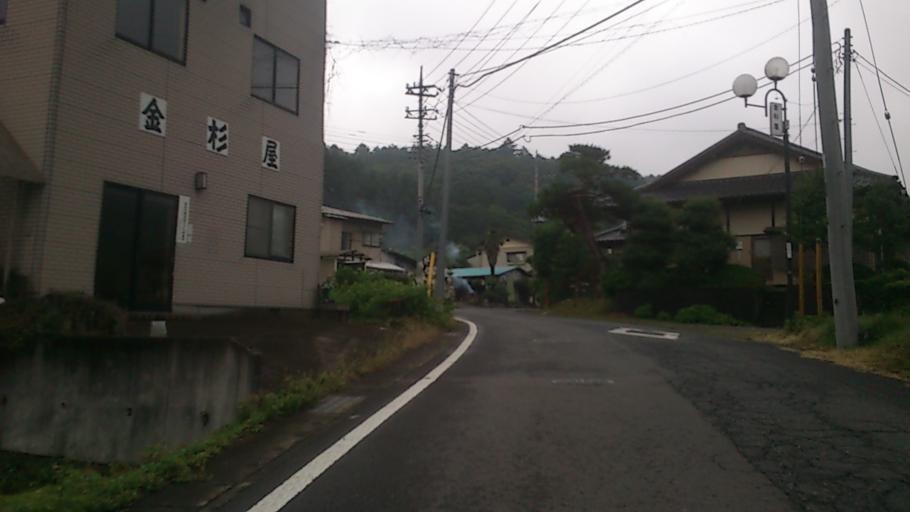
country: JP
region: Ibaraki
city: Daigo
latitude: 36.6645
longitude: 140.3094
